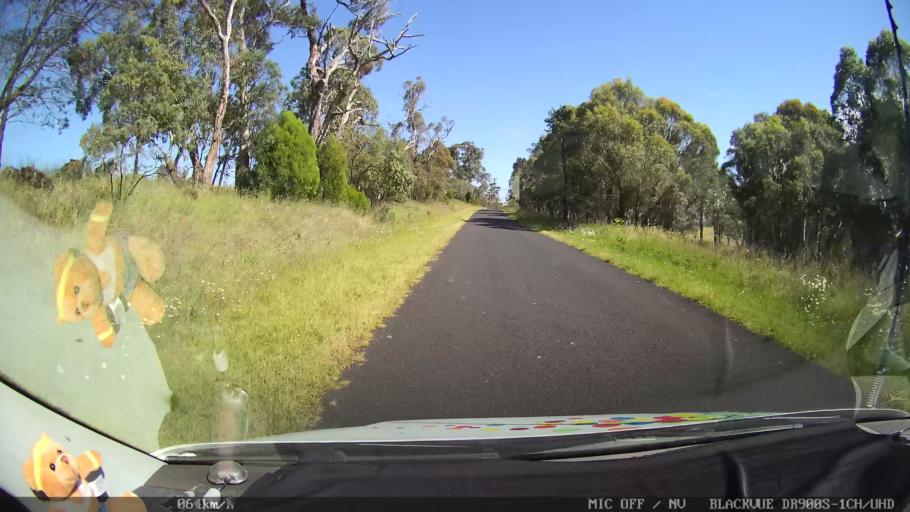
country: AU
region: New South Wales
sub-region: Guyra
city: Guyra
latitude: -30.0638
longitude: 151.6657
